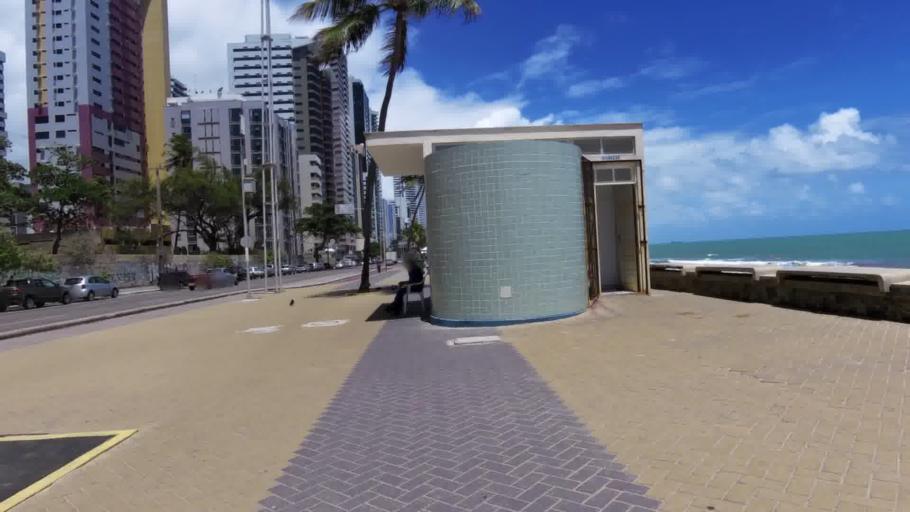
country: BR
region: Pernambuco
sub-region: Recife
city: Recife
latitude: -8.1391
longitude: -34.9025
